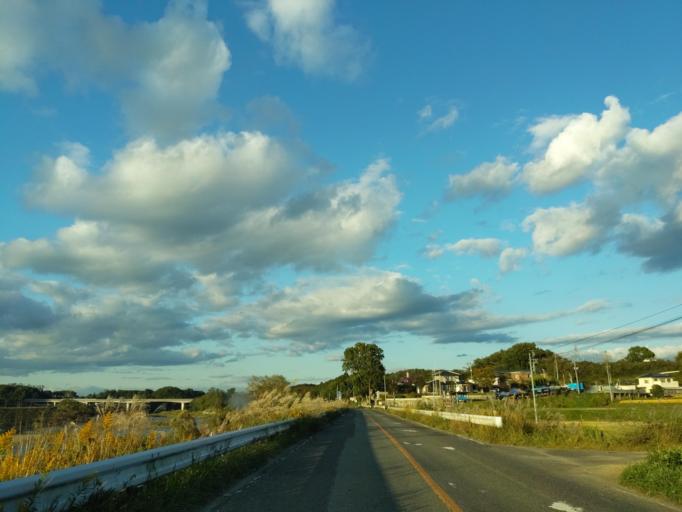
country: JP
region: Fukushima
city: Koriyama
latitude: 37.4349
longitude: 140.4212
